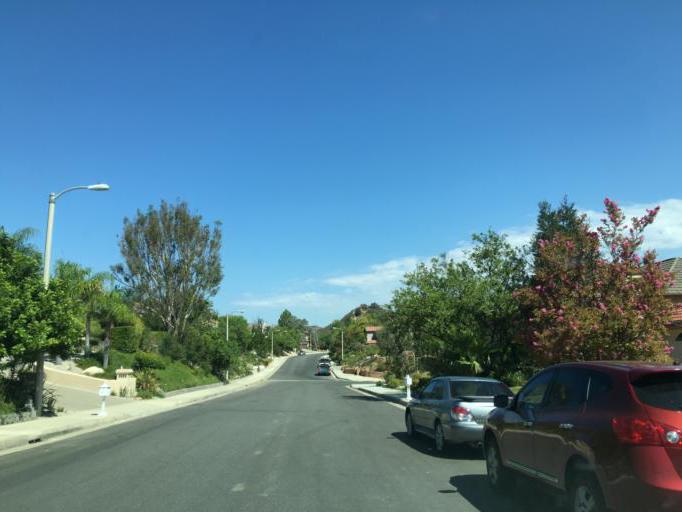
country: US
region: California
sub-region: Los Angeles County
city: Agoura
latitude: 34.1296
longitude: -118.7182
